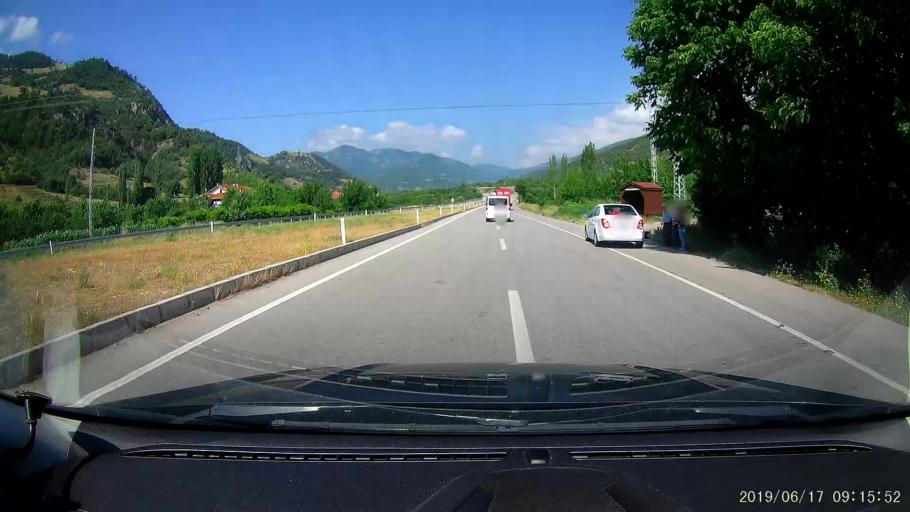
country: TR
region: Amasya
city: Akdag
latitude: 40.7465
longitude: 36.0258
